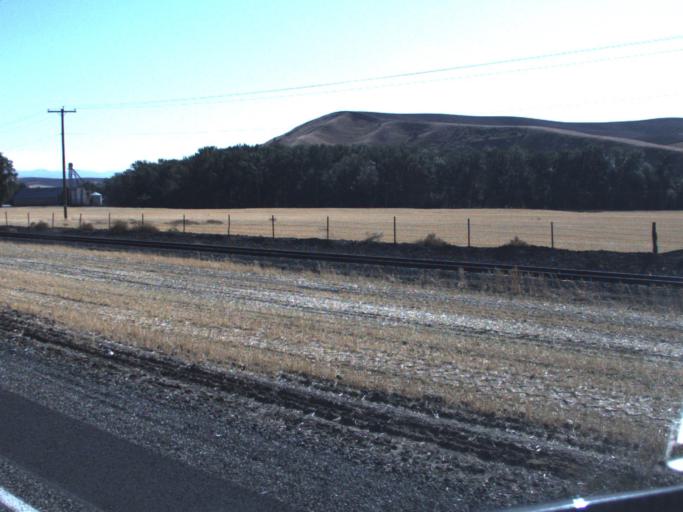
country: US
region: Washington
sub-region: Walla Walla County
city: Waitsburg
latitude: 46.2838
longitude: -118.2407
